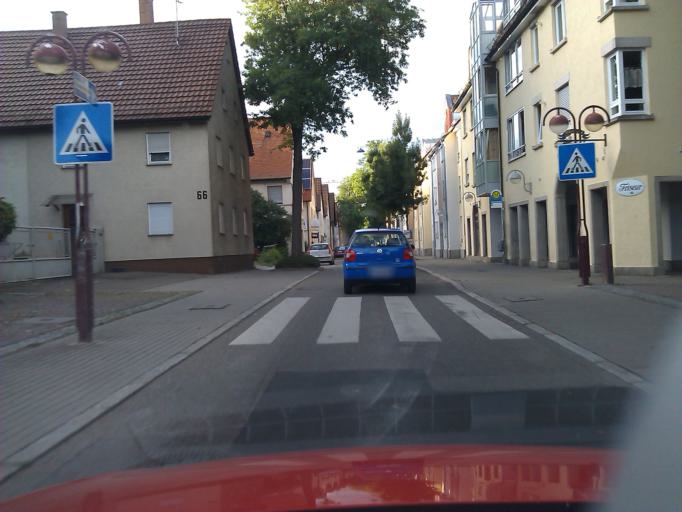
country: DE
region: Baden-Wuerttemberg
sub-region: Regierungsbezirk Stuttgart
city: Heilbronn
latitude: 49.1338
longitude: 9.1915
